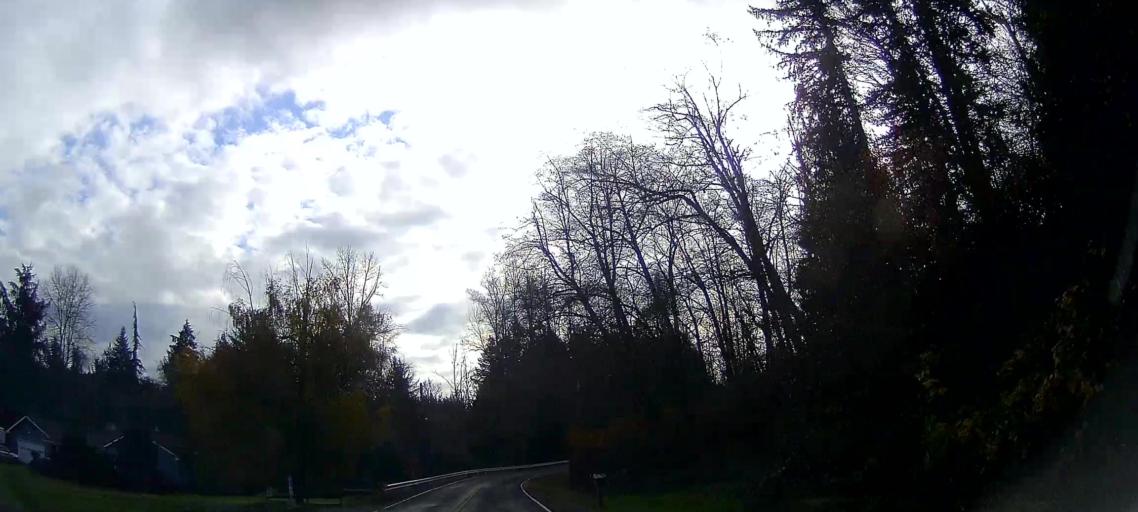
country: US
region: Washington
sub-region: Skagit County
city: Big Lake
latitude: 48.4141
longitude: -122.2063
